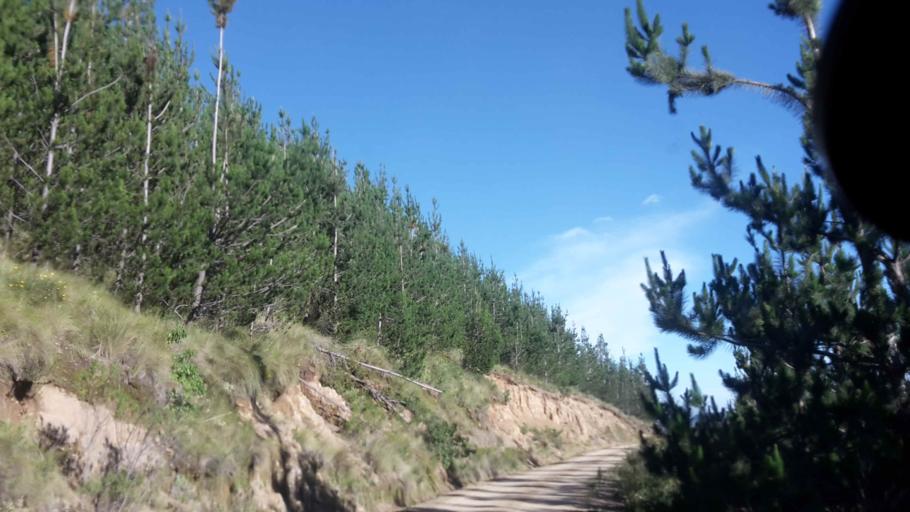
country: BO
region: Cochabamba
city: Arani
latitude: -17.7307
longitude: -65.6254
